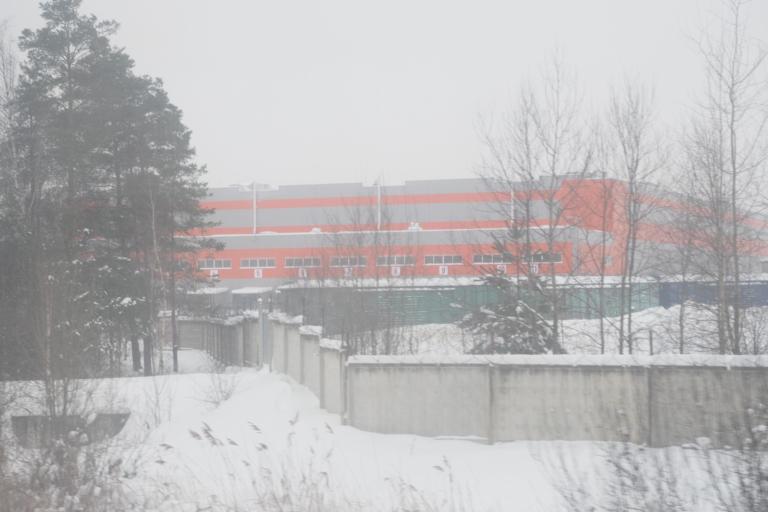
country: RU
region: Moskovskaya
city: Yegor'yevsk
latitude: 55.3718
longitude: 38.9992
